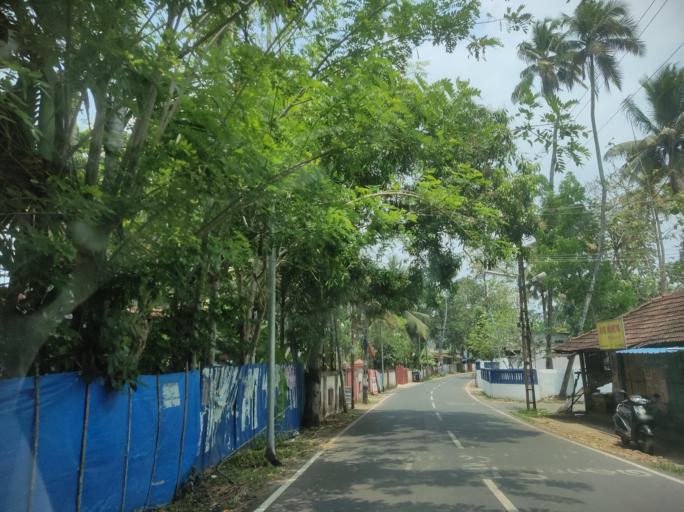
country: IN
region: Kerala
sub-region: Alappuzha
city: Vayalar
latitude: 9.7113
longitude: 76.3258
